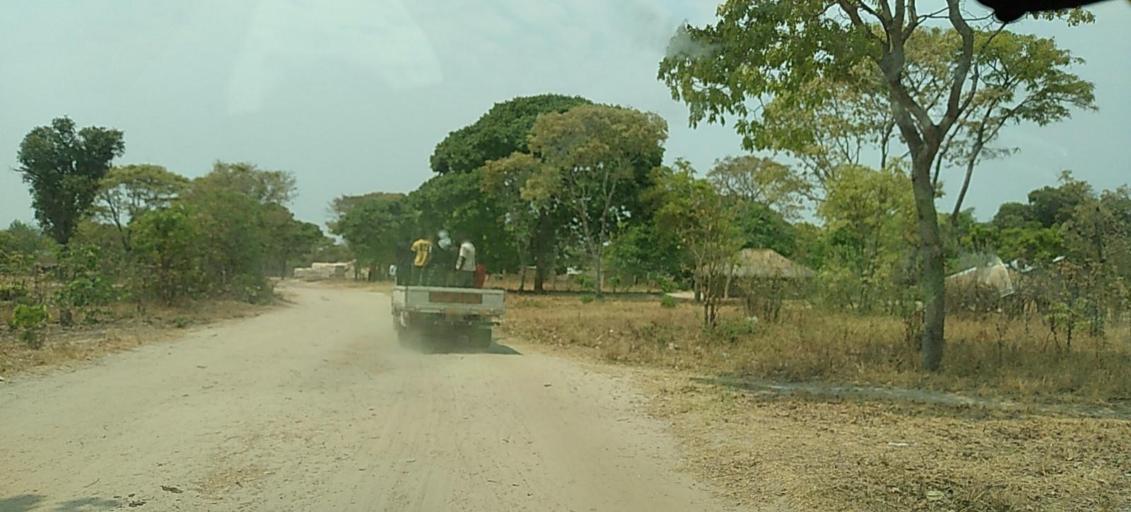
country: ZM
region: North-Western
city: Kabompo
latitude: -13.4899
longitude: 24.4625
